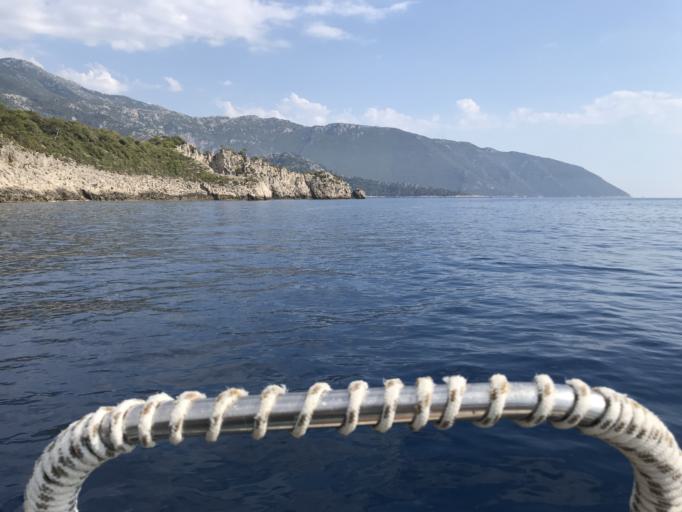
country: TR
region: Mugla
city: OEluedeniz
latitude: 36.4471
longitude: 29.1206
